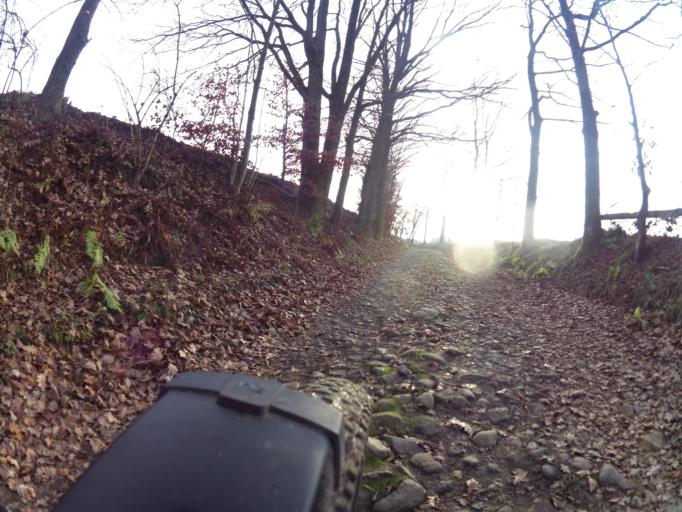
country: PL
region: West Pomeranian Voivodeship
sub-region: Powiat koszalinski
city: Polanow
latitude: 54.1537
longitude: 16.7300
